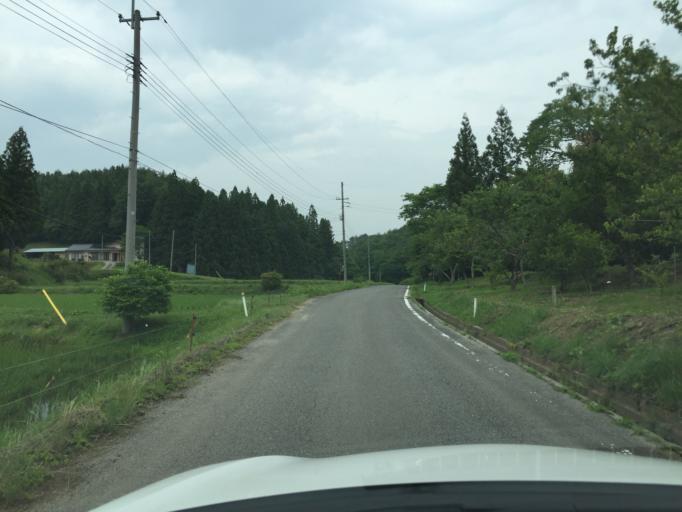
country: JP
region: Fukushima
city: Iwaki
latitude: 37.2009
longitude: 140.7214
